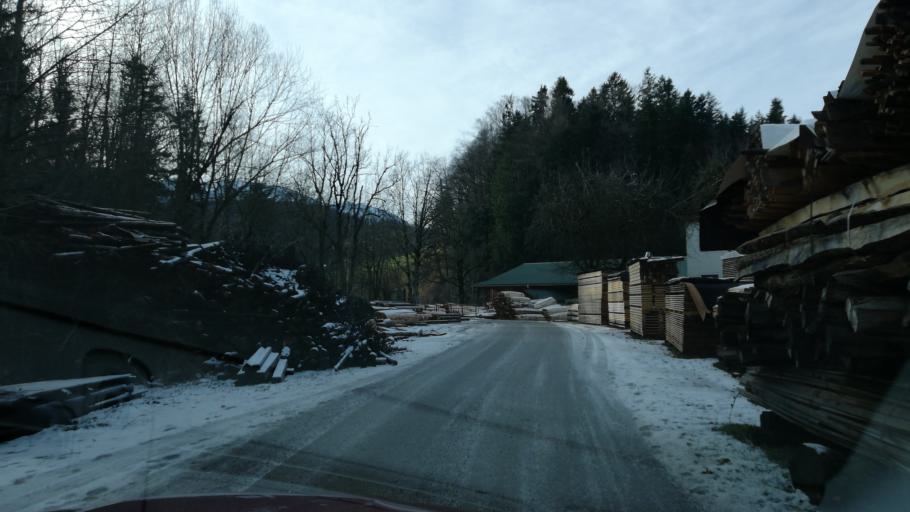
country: AT
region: Upper Austria
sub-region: Politischer Bezirk Kirchdorf an der Krems
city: Rossleithen
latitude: 47.7165
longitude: 14.3503
